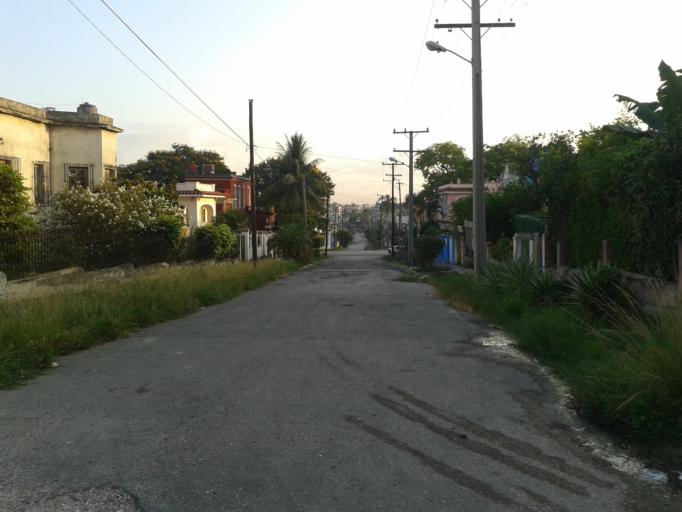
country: CU
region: La Habana
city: Diez de Octubre
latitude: 23.0935
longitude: -82.3698
